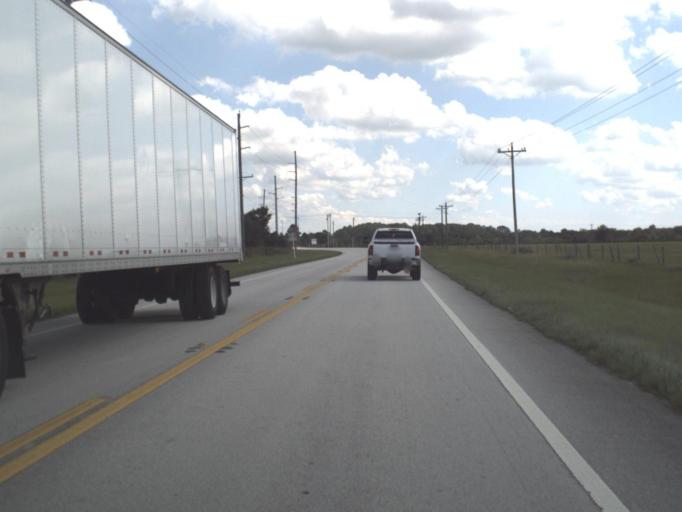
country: US
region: Florida
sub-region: Highlands County
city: Lake Placid
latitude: 27.4391
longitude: -81.2445
